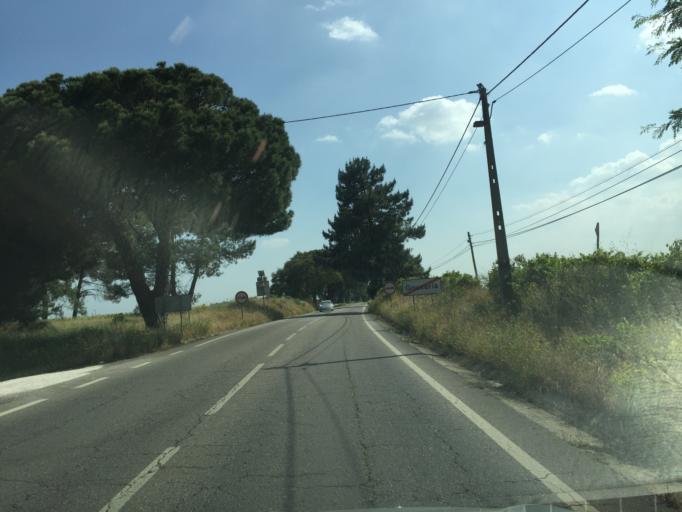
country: PT
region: Santarem
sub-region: Almeirim
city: Almeirim
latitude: 39.2275
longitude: -8.6063
